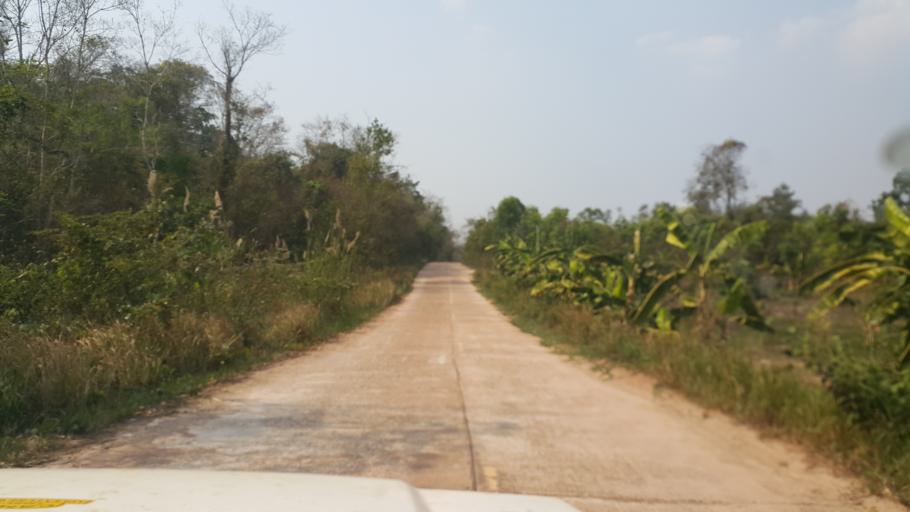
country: TH
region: Nakhon Phanom
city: Ban Phaeng
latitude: 17.9598
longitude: 104.1564
